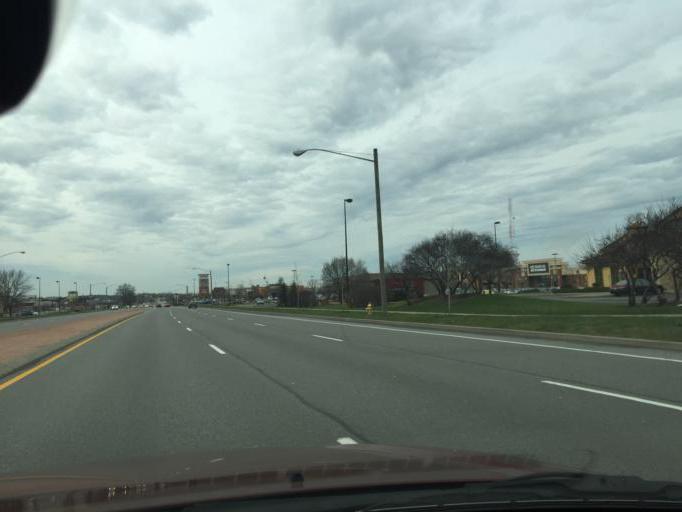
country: US
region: New York
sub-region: Monroe County
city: Rochester
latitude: 43.0872
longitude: -77.6206
